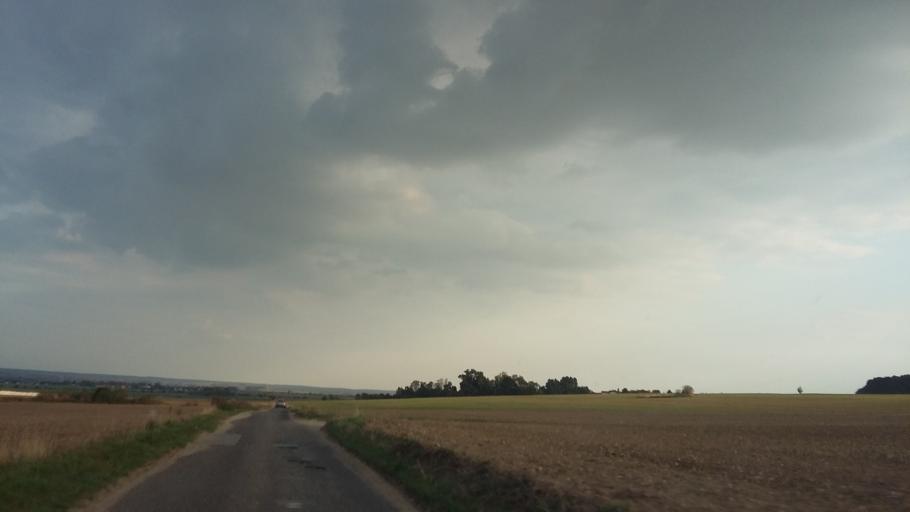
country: CZ
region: Central Bohemia
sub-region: Okres Mlada Boleslav
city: Mlada Boleslav
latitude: 50.3636
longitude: 14.8811
